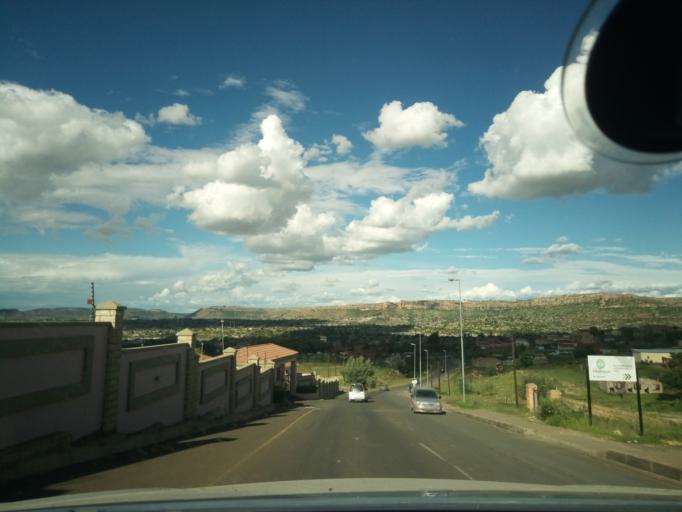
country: LS
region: Maseru
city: Maseru
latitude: -29.3279
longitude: 27.4962
